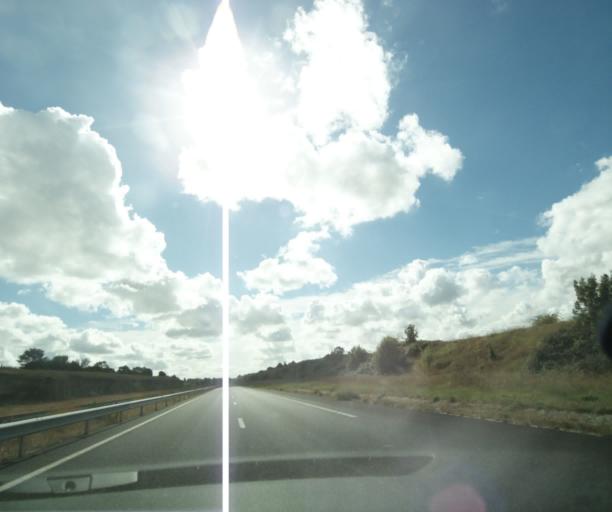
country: FR
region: Poitou-Charentes
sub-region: Departement de la Charente-Maritime
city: Saint-Savinien
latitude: 45.8525
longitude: -0.7241
